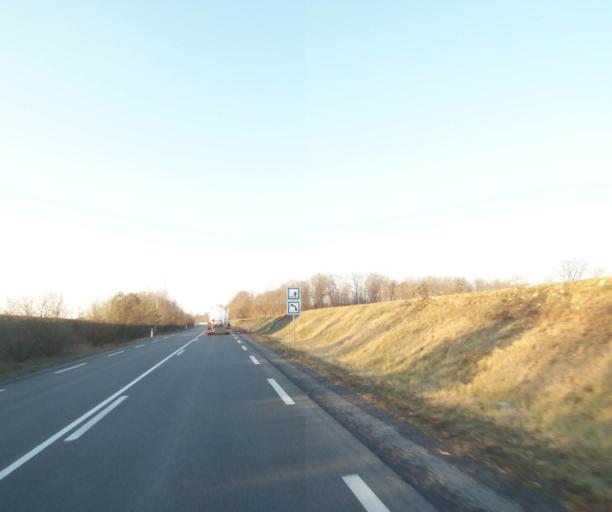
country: FR
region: Champagne-Ardenne
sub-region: Departement de la Haute-Marne
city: Bienville
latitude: 48.5489
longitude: 5.0657
